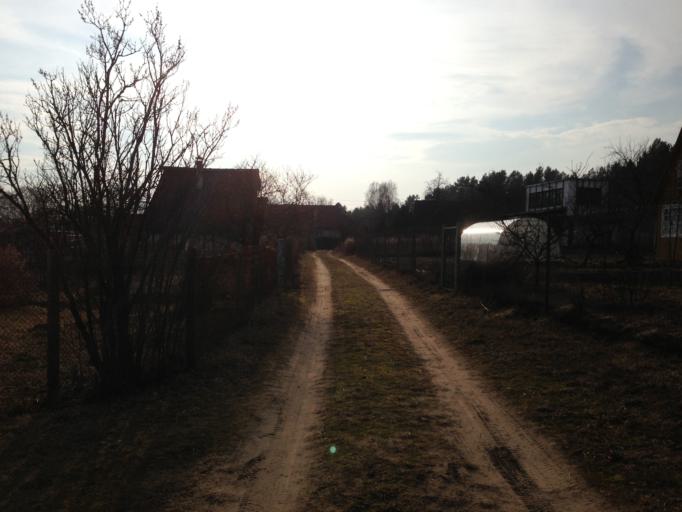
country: LT
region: Alytaus apskritis
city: Druskininkai
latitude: 53.9212
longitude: 24.1905
